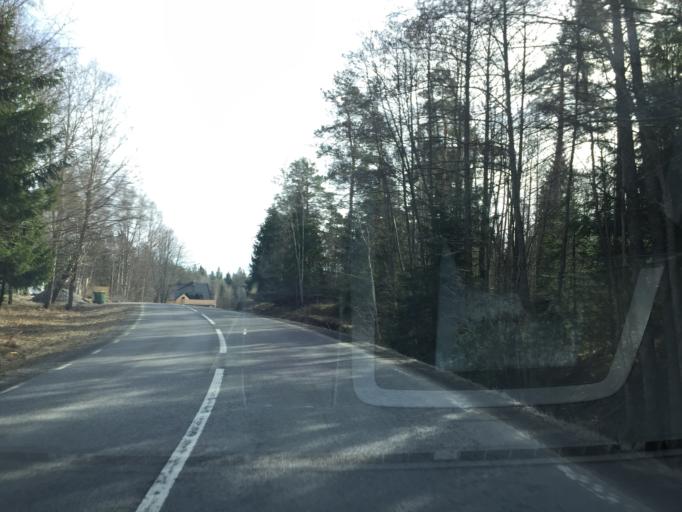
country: SE
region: Stockholm
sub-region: Huddinge Kommun
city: Huddinge
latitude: 59.1262
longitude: 18.0032
